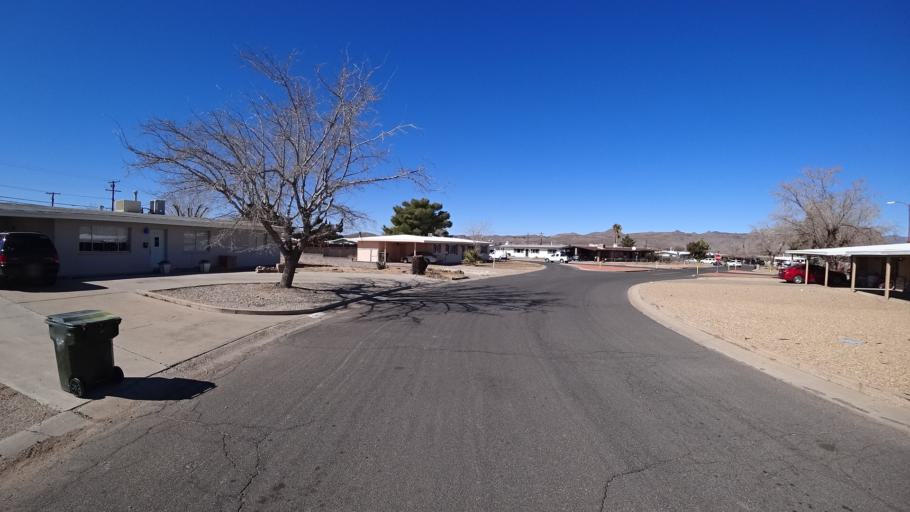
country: US
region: Arizona
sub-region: Mohave County
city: Kingman
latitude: 35.2109
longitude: -114.0229
